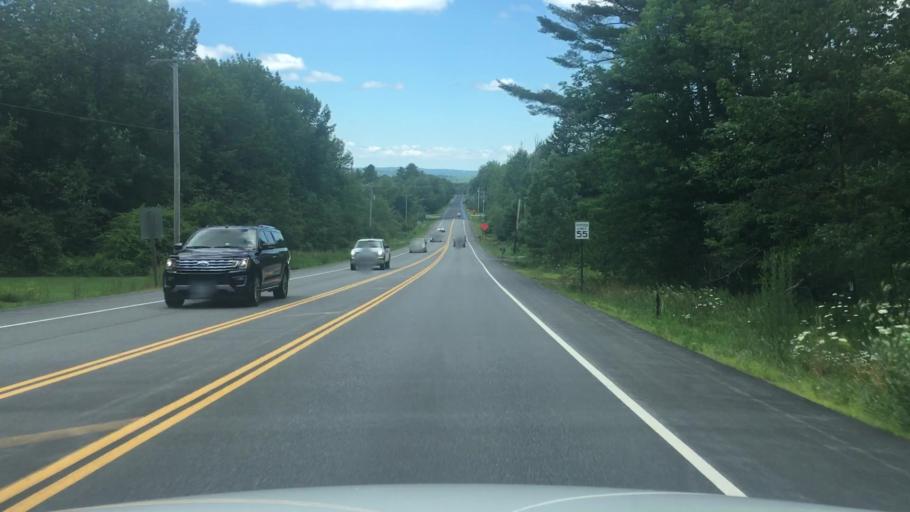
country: US
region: Maine
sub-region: Waldo County
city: Searsmont
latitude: 44.3976
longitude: -69.1400
